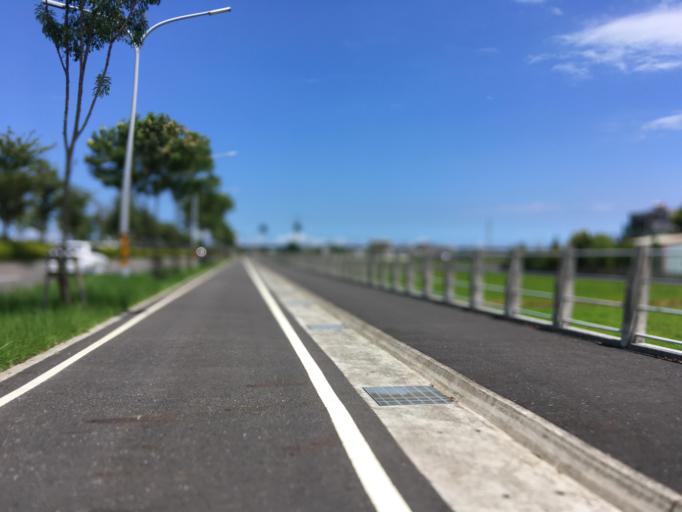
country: TW
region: Taiwan
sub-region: Yilan
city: Yilan
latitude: 24.6934
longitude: 121.7839
